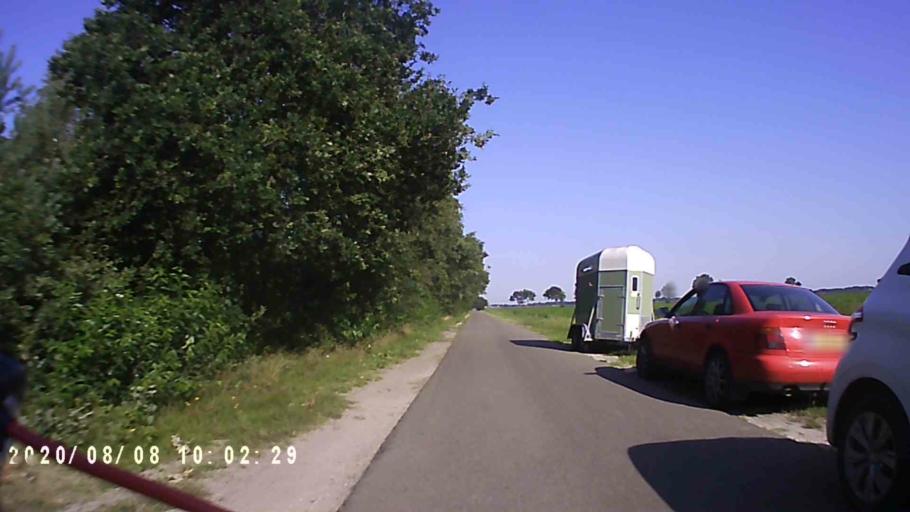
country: NL
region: Groningen
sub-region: Gemeente Leek
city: Leek
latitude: 53.1061
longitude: 6.3857
